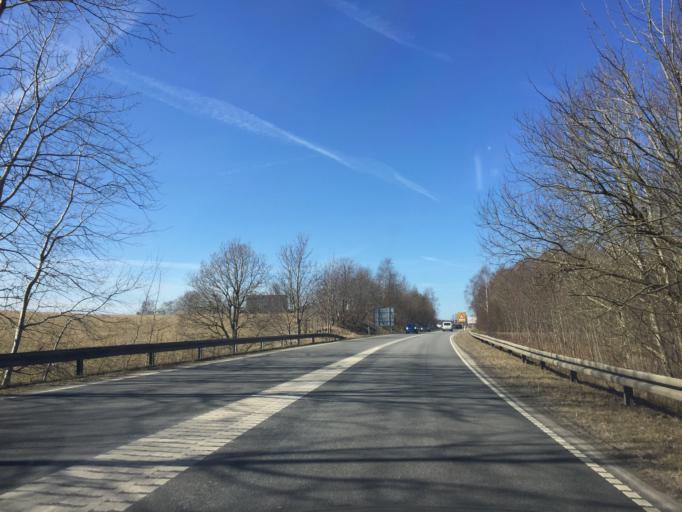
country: DK
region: Capital Region
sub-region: Fredensborg Kommune
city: Humlebaek
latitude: 55.9853
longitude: 12.5077
